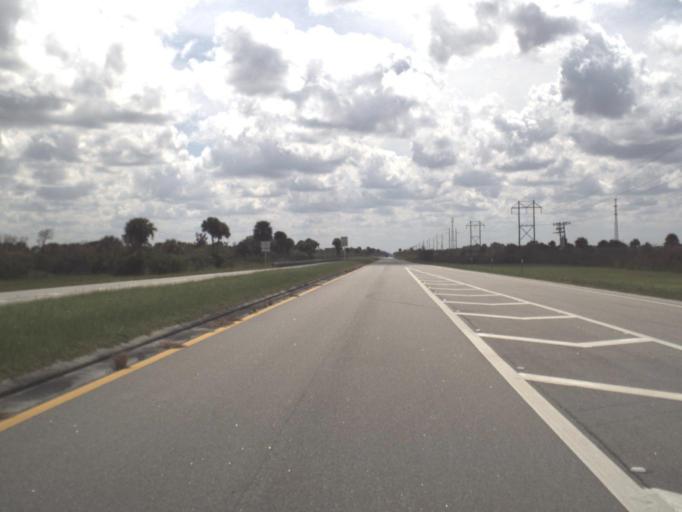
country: US
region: Florida
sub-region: Collier County
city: Immokalee
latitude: 26.1504
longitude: -81.3451
